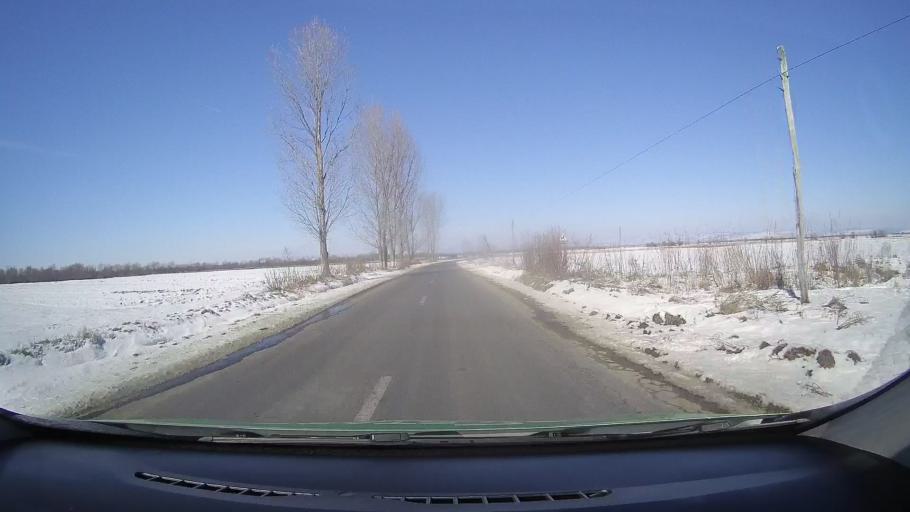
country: RO
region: Brasov
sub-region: Comuna Harseni
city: Harseni
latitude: 45.7332
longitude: 25.0267
